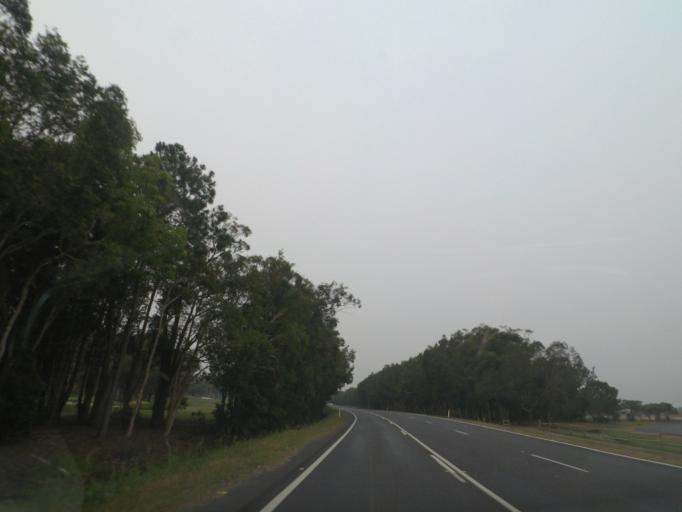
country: AU
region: New South Wales
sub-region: Coffs Harbour
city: Coffs Harbour
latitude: -30.3149
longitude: 153.1137
